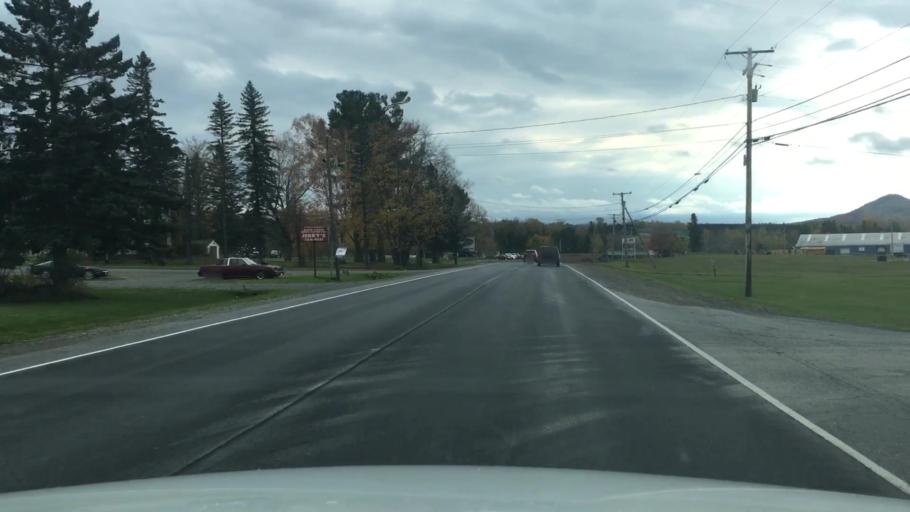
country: US
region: Maine
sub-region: Aroostook County
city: Presque Isle
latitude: 46.6541
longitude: -68.0050
